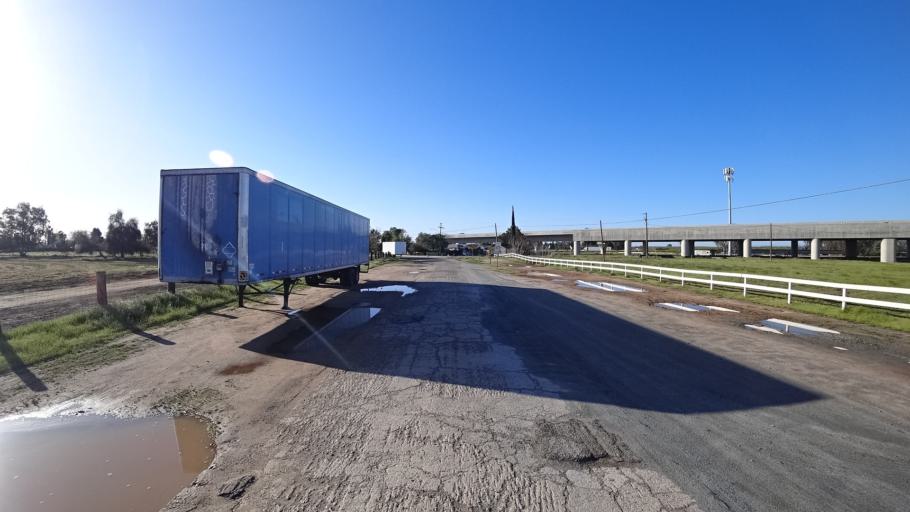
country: US
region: California
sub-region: Fresno County
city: Biola
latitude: 36.8394
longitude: -119.9218
